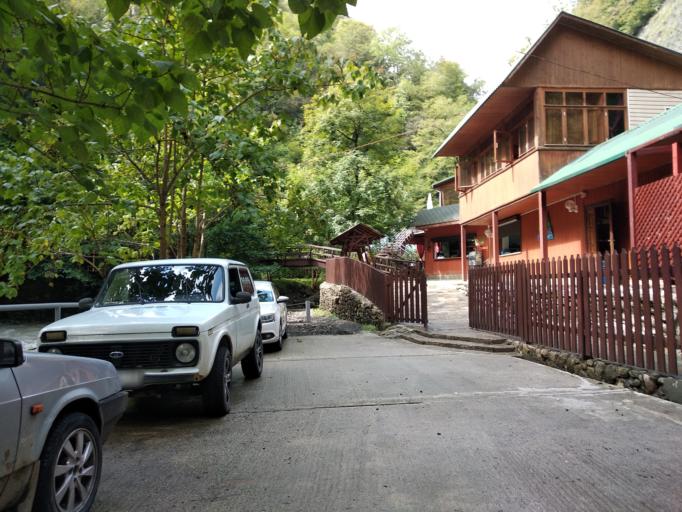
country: RU
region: Krasnodarskiy
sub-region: Sochi City
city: Sochi
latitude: 43.6356
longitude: 39.8170
